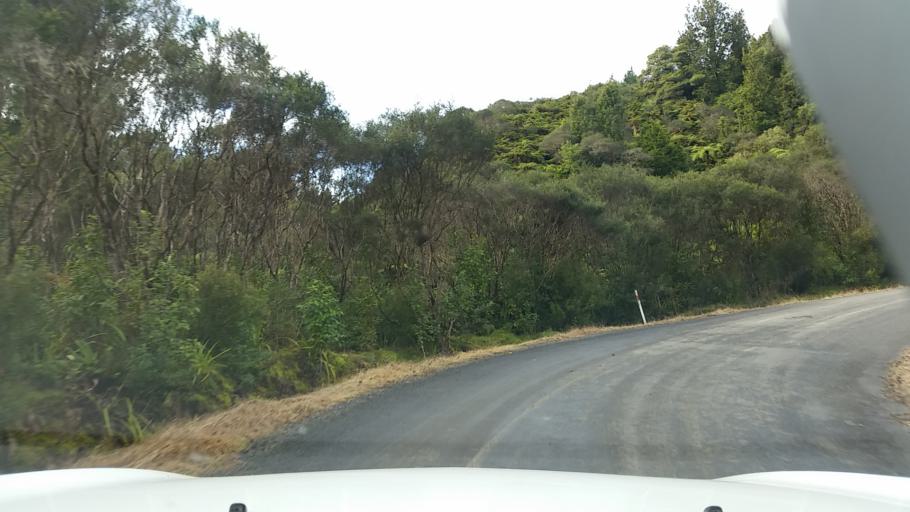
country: NZ
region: Taranaki
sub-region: New Plymouth District
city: Waitara
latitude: -38.9099
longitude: 174.7665
